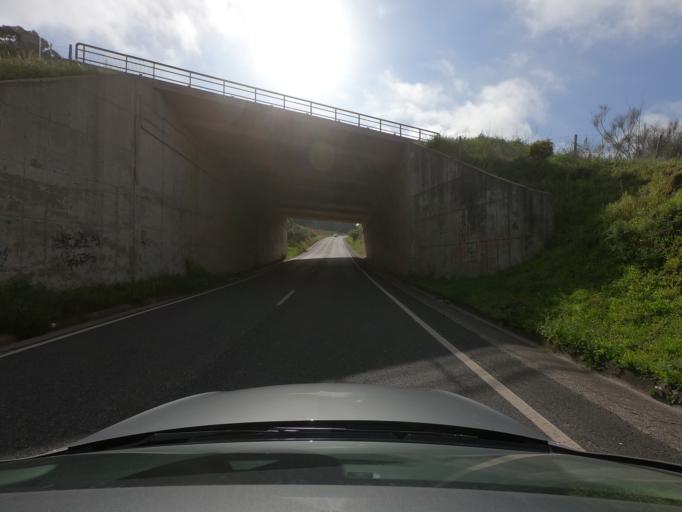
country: PT
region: Lisbon
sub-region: Oeiras
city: Barcarena
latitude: 38.7287
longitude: -9.2744
